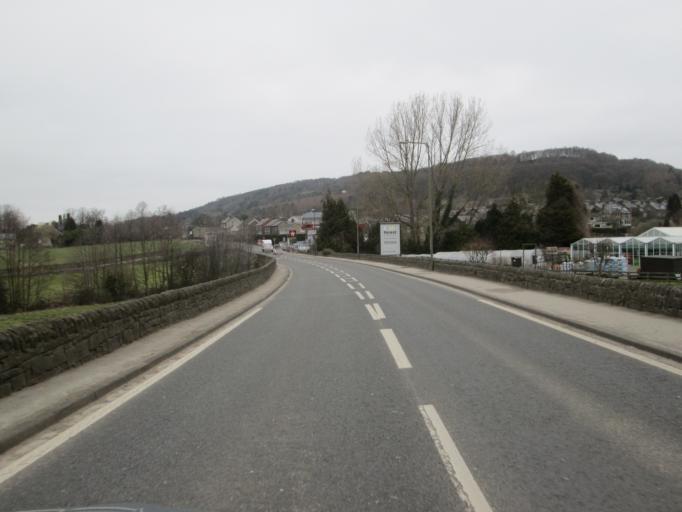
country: GB
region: England
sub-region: Derbyshire
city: Matlock
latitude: 53.1595
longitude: -1.5866
